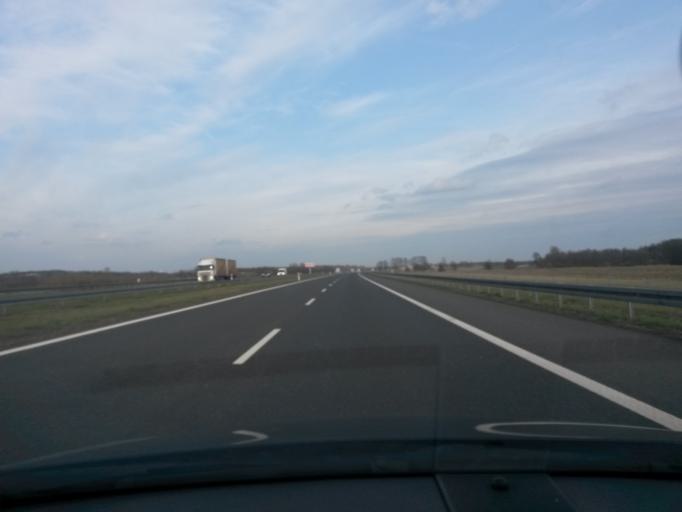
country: PL
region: Lodz Voivodeship
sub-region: Powiat zgierski
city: Parzeczew
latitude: 51.9397
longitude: 19.2229
